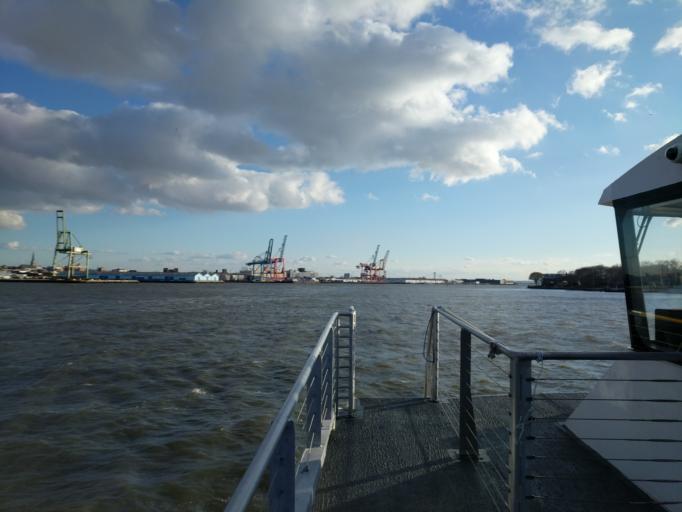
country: US
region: New York
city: New York City
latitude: 40.6946
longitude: -74.0083
